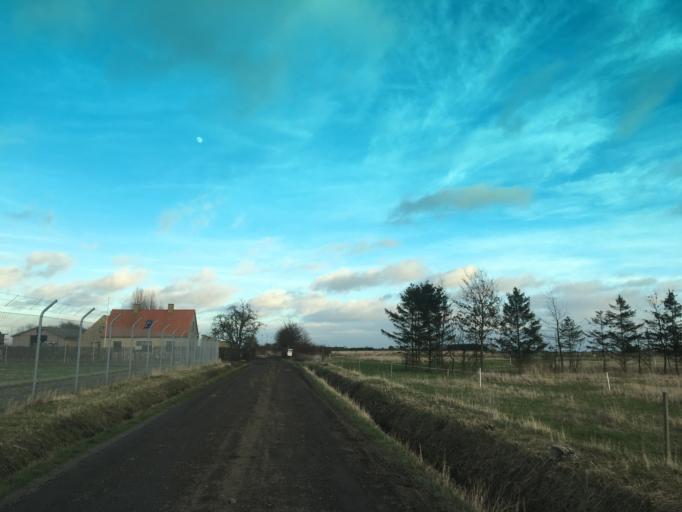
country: DK
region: Capital Region
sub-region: Tarnby Kommune
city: Tarnby
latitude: 55.5863
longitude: 12.6030
